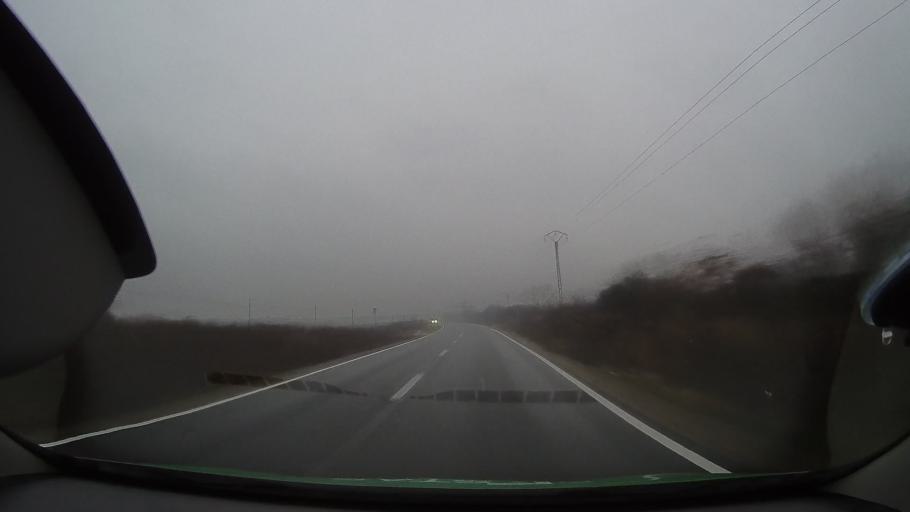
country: RO
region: Bihor
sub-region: Comuna Tinca
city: Tinca
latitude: 46.7263
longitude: 21.9446
